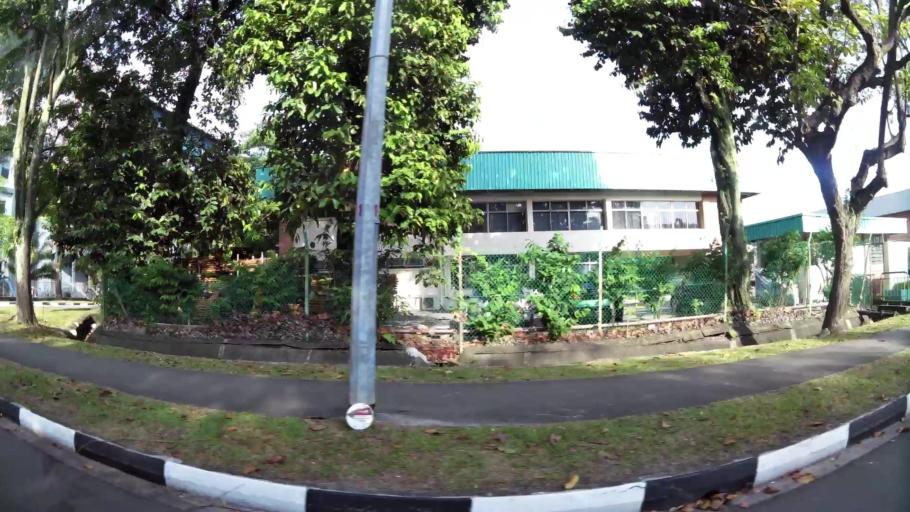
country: MY
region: Johor
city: Johor Bahru
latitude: 1.3200
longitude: 103.6583
